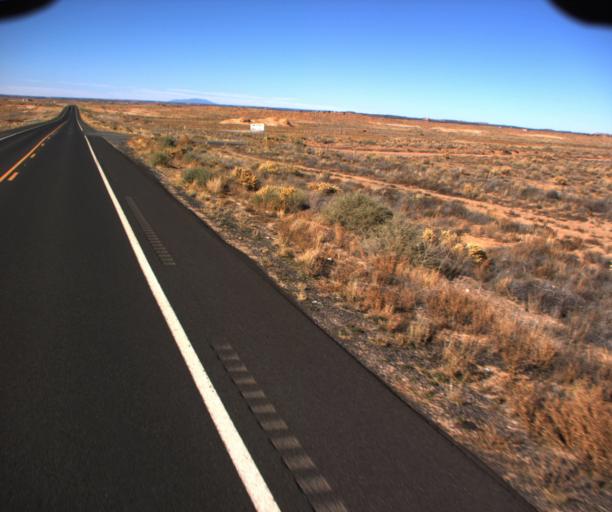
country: US
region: Arizona
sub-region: Coconino County
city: Kaibito
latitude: 36.4727
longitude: -110.6986
